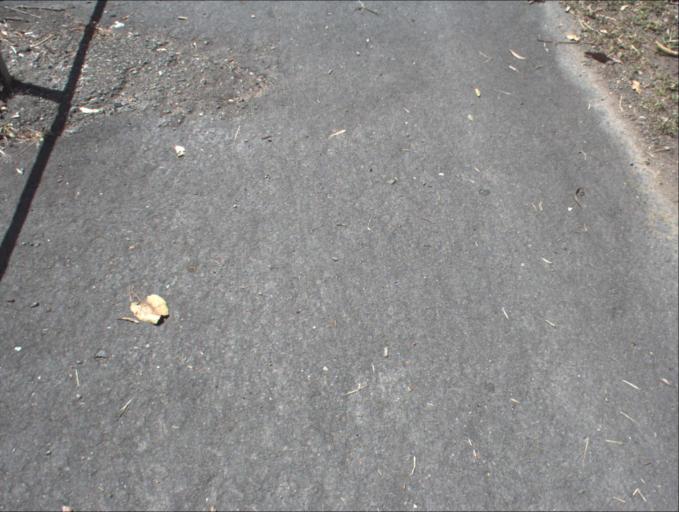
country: AU
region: Queensland
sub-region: Logan
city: Windaroo
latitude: -27.7289
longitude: 153.1922
